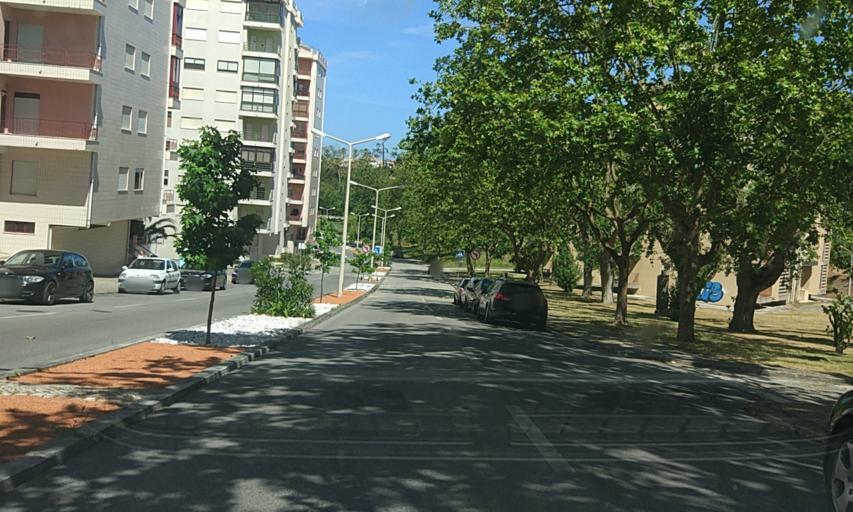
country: PT
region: Coimbra
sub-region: Figueira da Foz
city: Figueira da Foz
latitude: 40.1542
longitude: -8.8580
